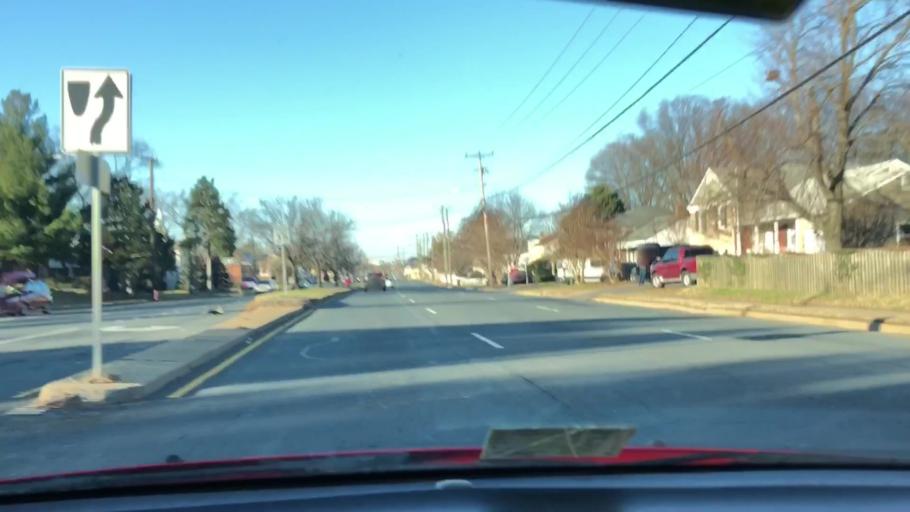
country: US
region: Virginia
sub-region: Fairfax County
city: Franconia
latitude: 38.7828
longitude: -77.1430
